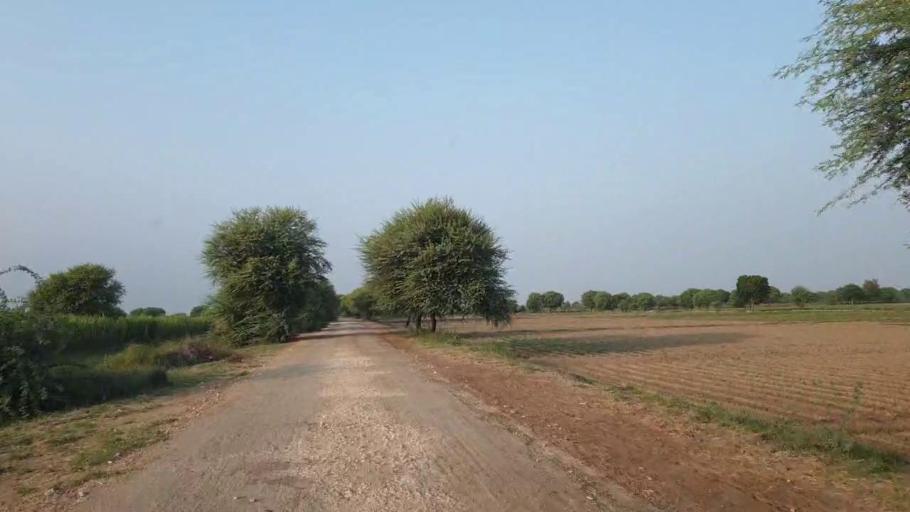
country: PK
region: Sindh
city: Rajo Khanani
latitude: 25.0413
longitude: 68.9644
